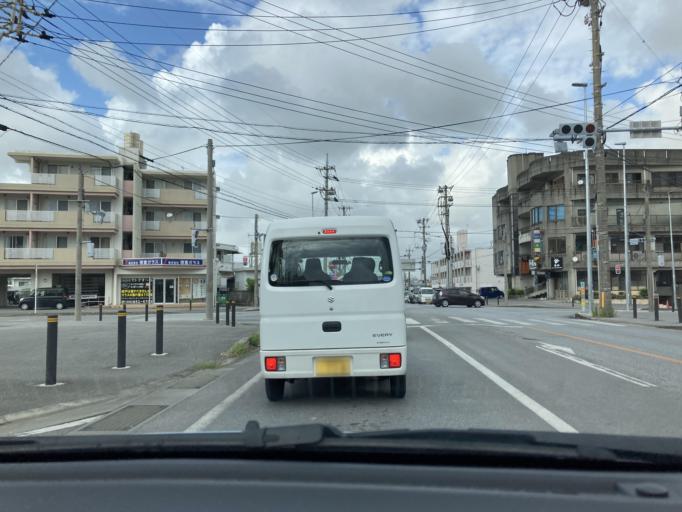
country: JP
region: Okinawa
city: Itoman
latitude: 26.1342
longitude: 127.6867
